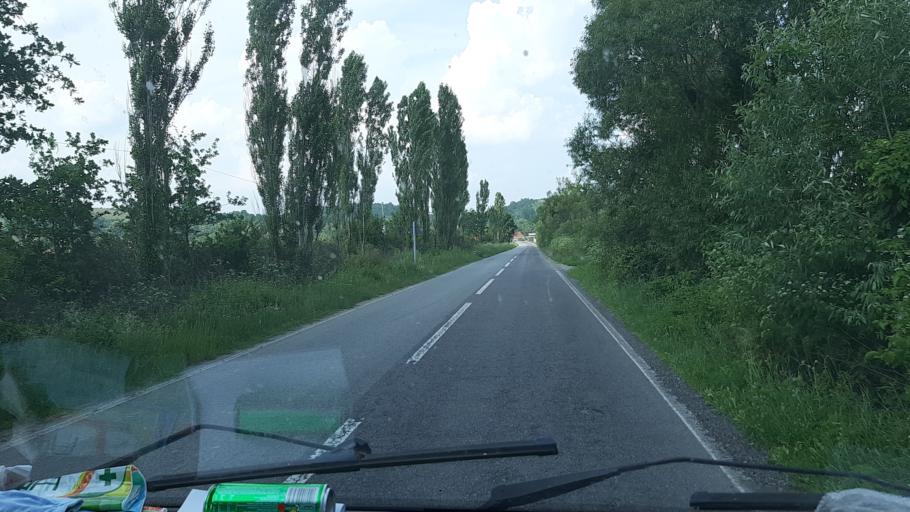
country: RO
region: Caras-Severin
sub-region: Comuna Farliug
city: Farliug
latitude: 45.5043
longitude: 21.8723
